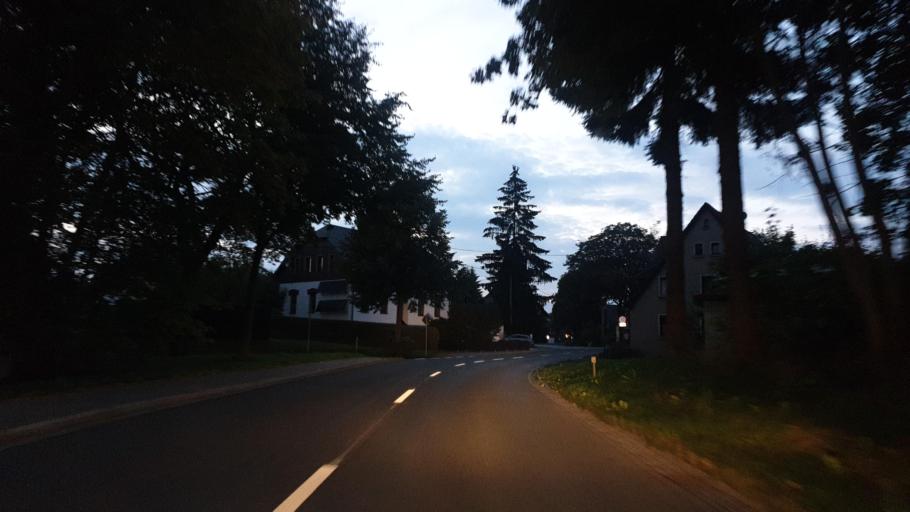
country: DE
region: Saxony
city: Auerbach
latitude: 50.5074
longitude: 12.4249
